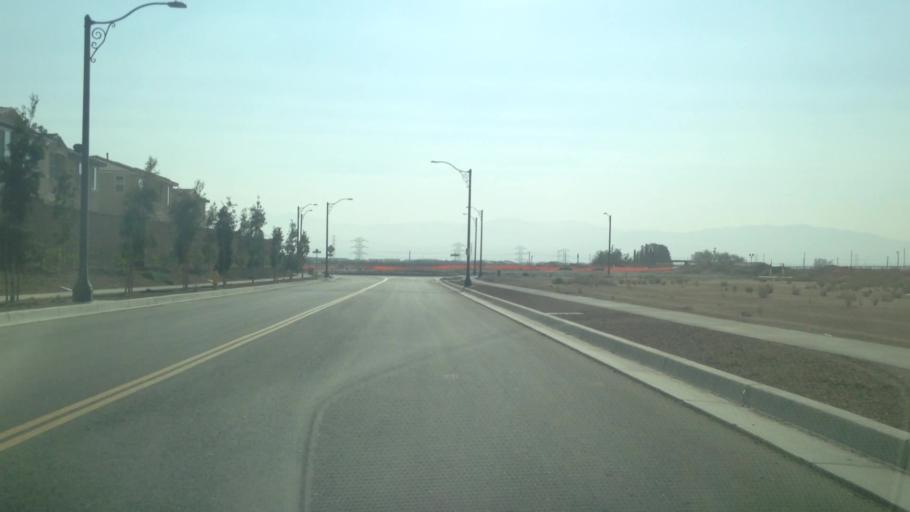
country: US
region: California
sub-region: Riverside County
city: Mira Loma
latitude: 33.9938
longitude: -117.5840
